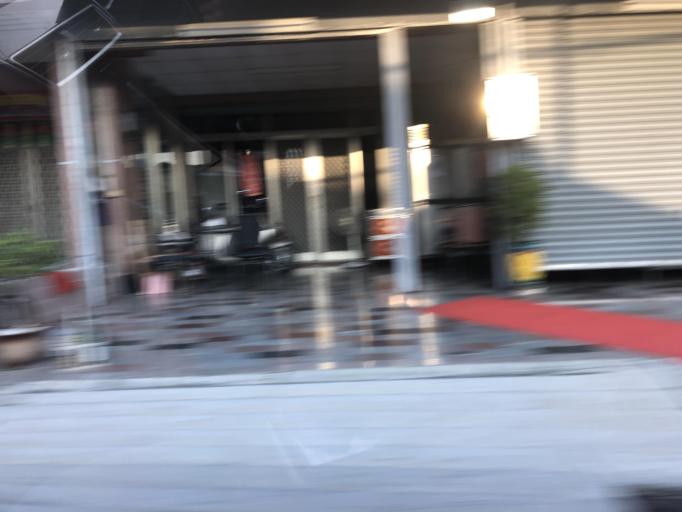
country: TW
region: Taiwan
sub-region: Tainan
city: Tainan
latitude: 23.1278
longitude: 120.2509
